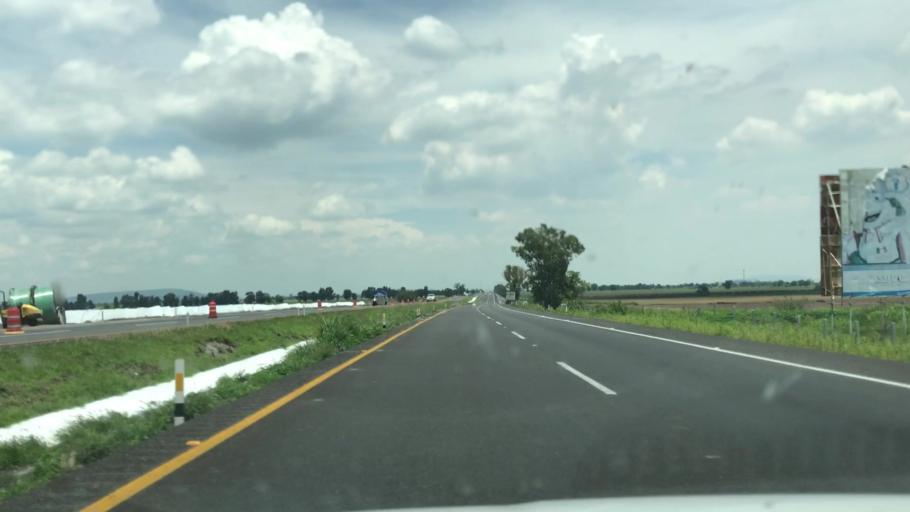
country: MX
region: Guanajuato
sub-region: Salamanca
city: San Vicente de Flores
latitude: 20.6397
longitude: -101.2644
